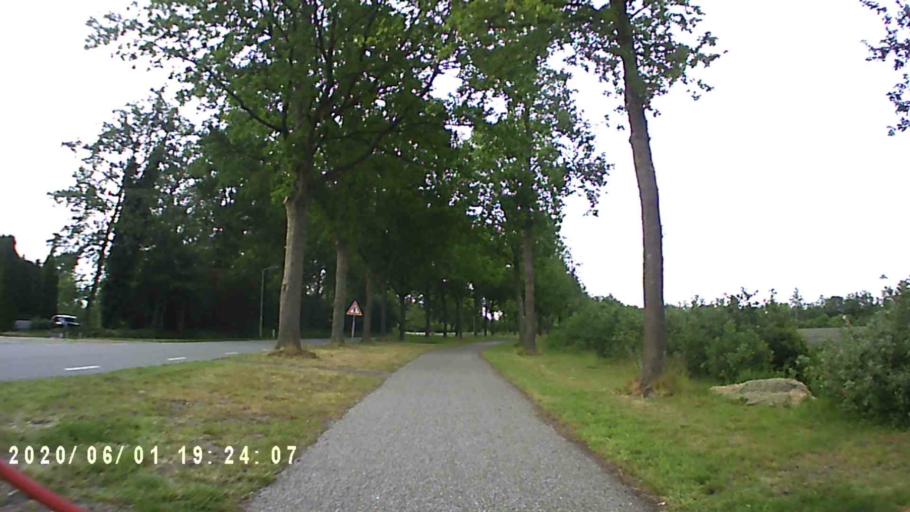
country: NL
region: Friesland
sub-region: Gemeente Achtkarspelen
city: Drogeham
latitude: 53.2050
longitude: 6.1276
